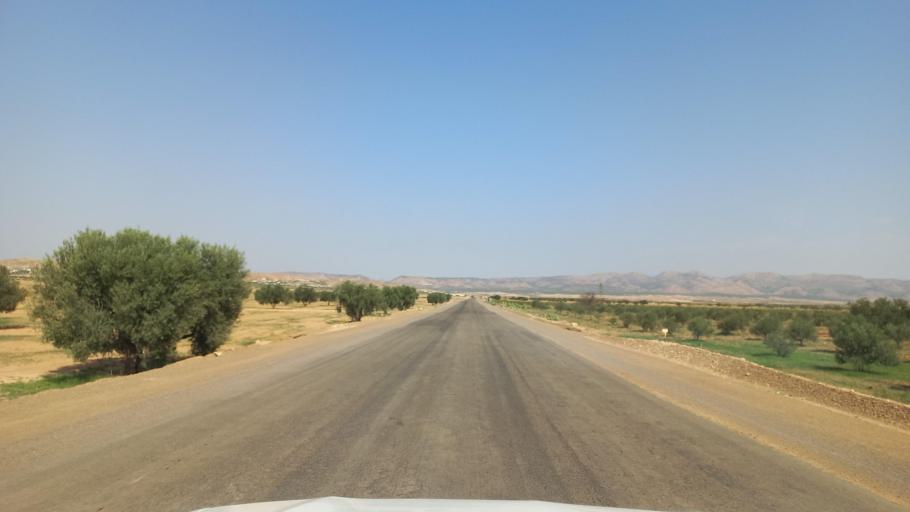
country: TN
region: Al Qasrayn
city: Sbiba
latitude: 35.3646
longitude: 9.0420
